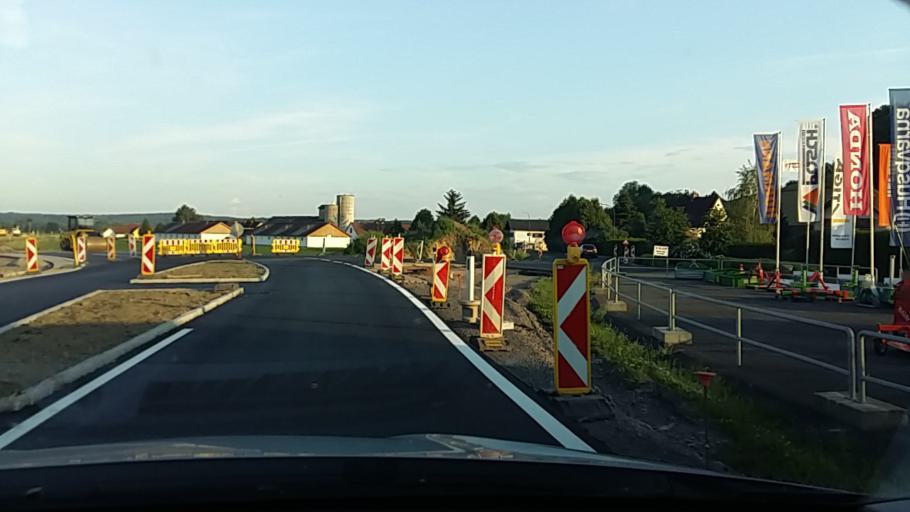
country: AT
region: Styria
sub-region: Politischer Bezirk Suedoststeiermark
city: Fehring
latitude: 46.9580
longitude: 16.0154
